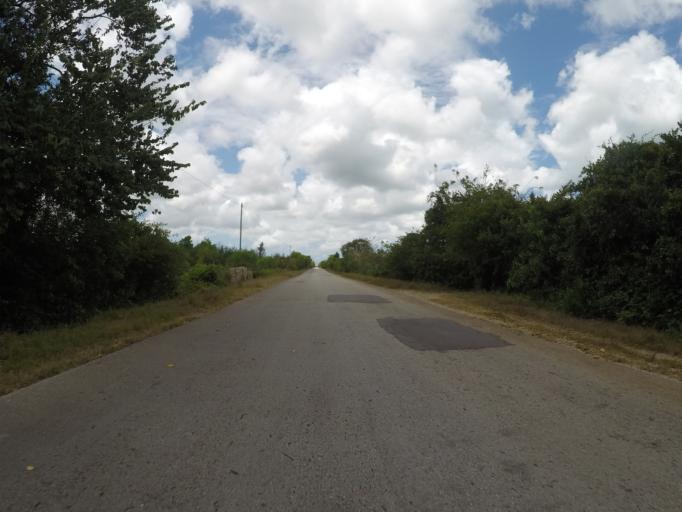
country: TZ
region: Zanzibar Central/South
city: Mahonda
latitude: -6.3203
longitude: 39.4343
